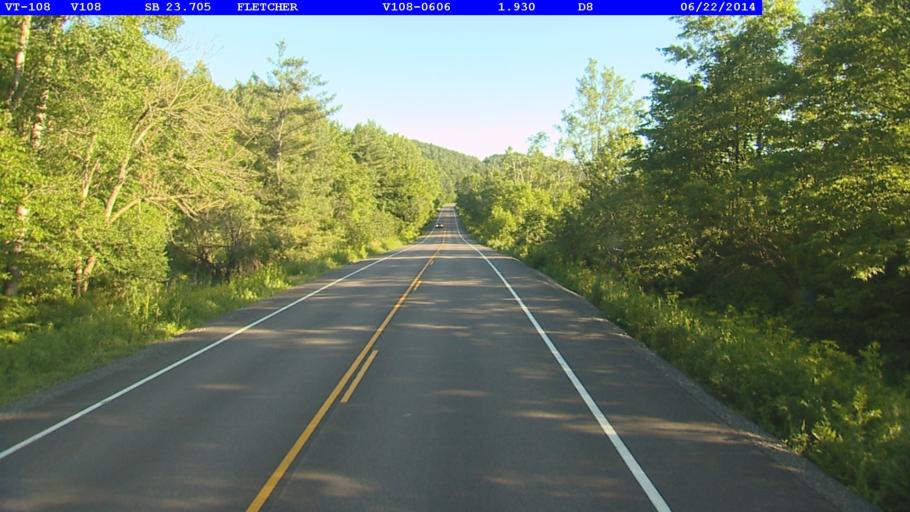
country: US
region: Vermont
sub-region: Lamoille County
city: Johnson
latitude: 44.7281
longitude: -72.8296
